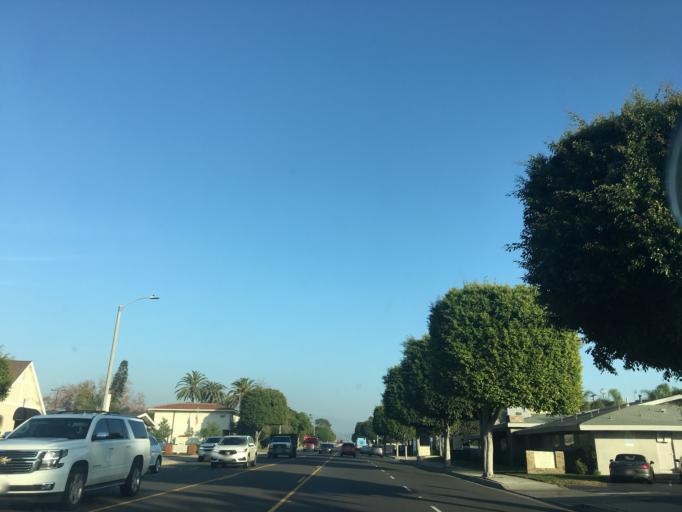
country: US
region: California
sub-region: Orange County
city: Orange
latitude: 33.7878
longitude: -117.8432
